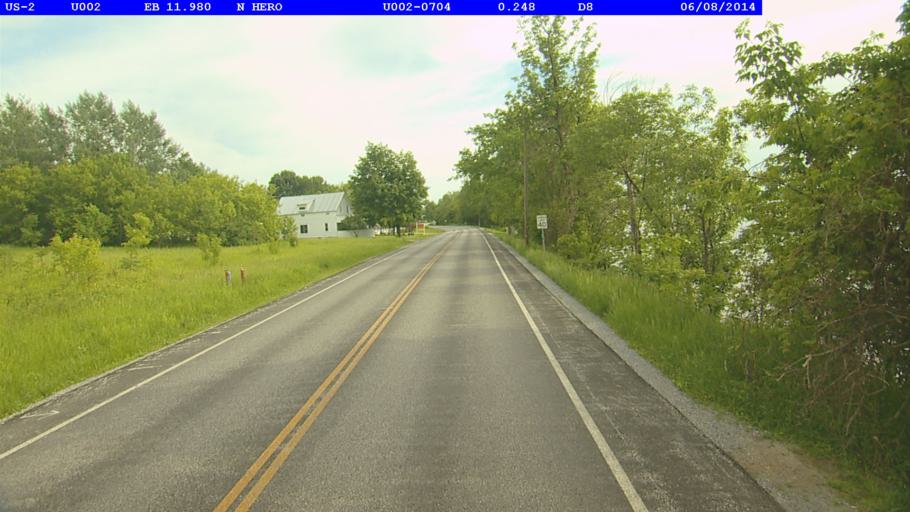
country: US
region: Vermont
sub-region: Grand Isle County
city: North Hero
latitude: 44.8827
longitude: -73.2720
